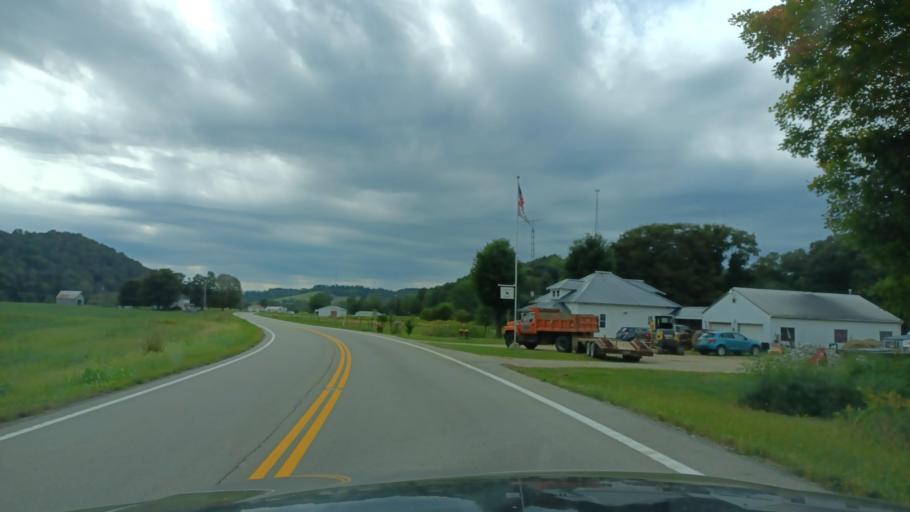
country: US
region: Ohio
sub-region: Vinton County
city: McArthur
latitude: 39.2730
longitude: -82.6597
